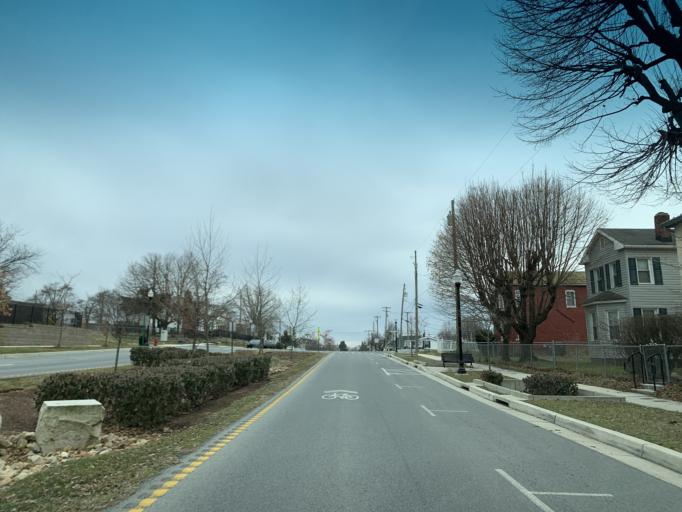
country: US
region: West Virginia
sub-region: Jefferson County
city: Ranson
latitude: 39.2993
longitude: -77.8588
